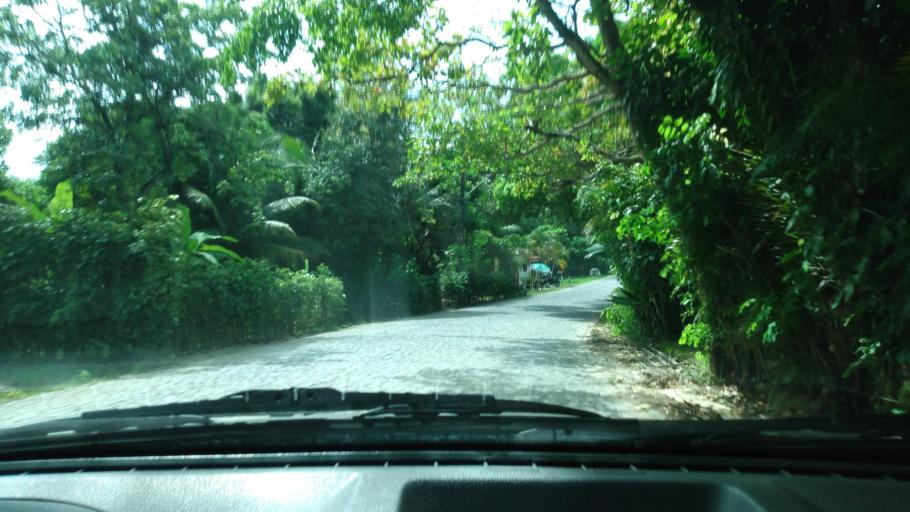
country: BR
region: Pernambuco
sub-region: Cabo De Santo Agostinho
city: Cabo
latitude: -8.3514
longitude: -34.9524
